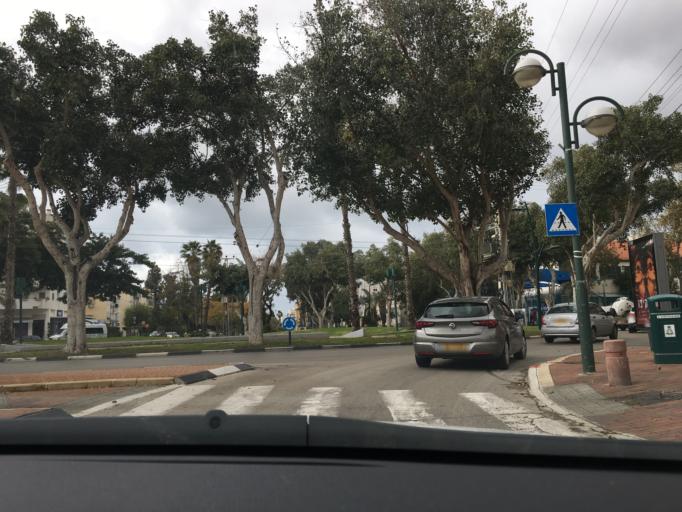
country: IL
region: Tel Aviv
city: Ramat HaSharon
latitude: 32.1440
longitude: 34.8447
